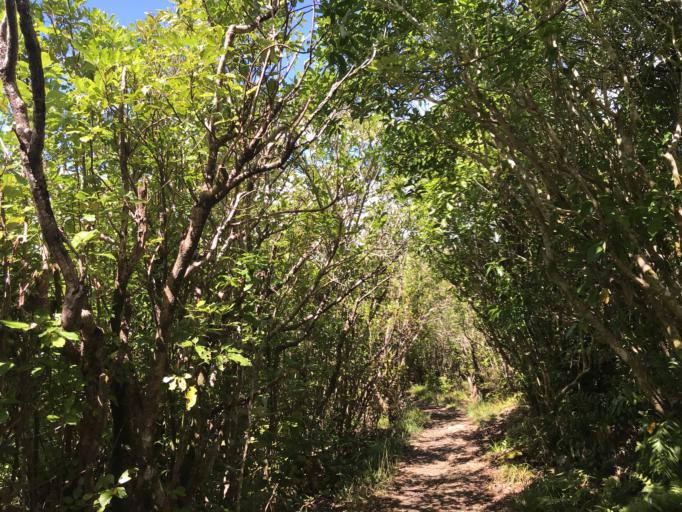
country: NZ
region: Marlborough
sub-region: Marlborough District
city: Picton
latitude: -41.2068
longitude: 174.0233
